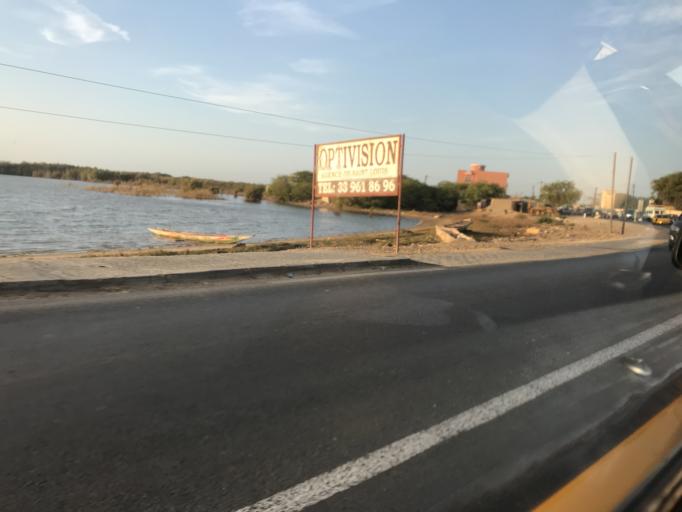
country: SN
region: Saint-Louis
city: Saint-Louis
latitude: 16.0269
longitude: -16.4767
